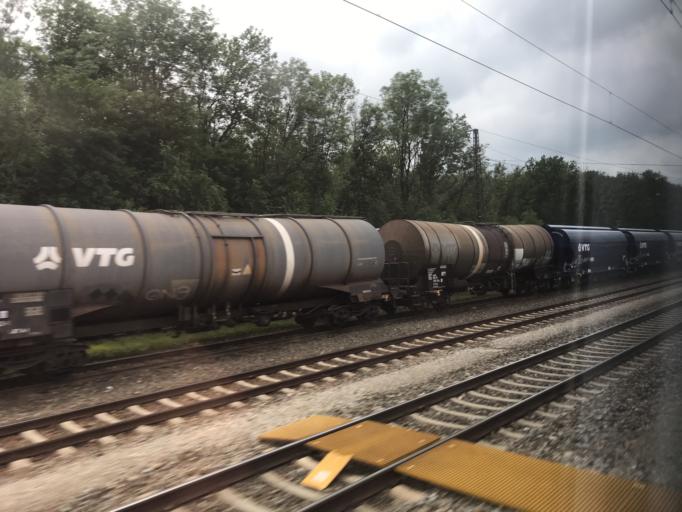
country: DE
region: Bavaria
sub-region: Swabia
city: Offingen
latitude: 48.4831
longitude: 10.3455
